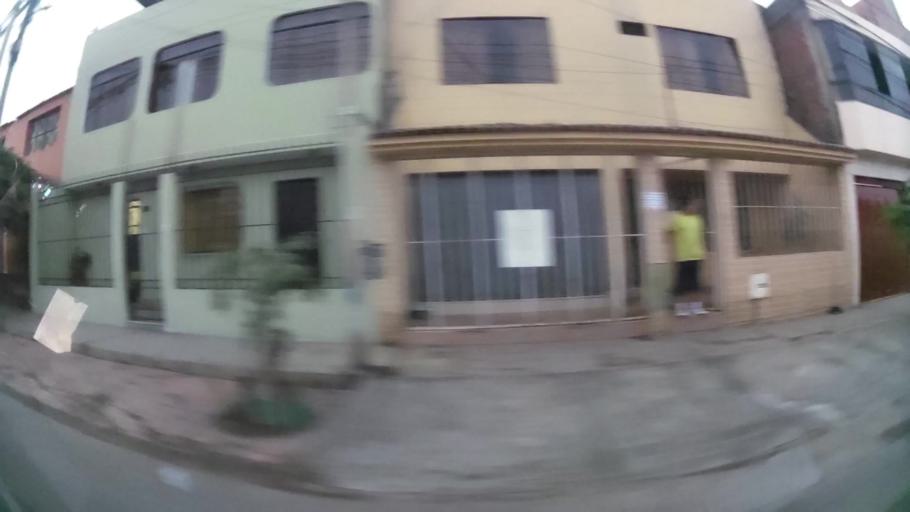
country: PE
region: Lima
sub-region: Lima
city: Surco
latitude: -12.1486
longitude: -76.9718
